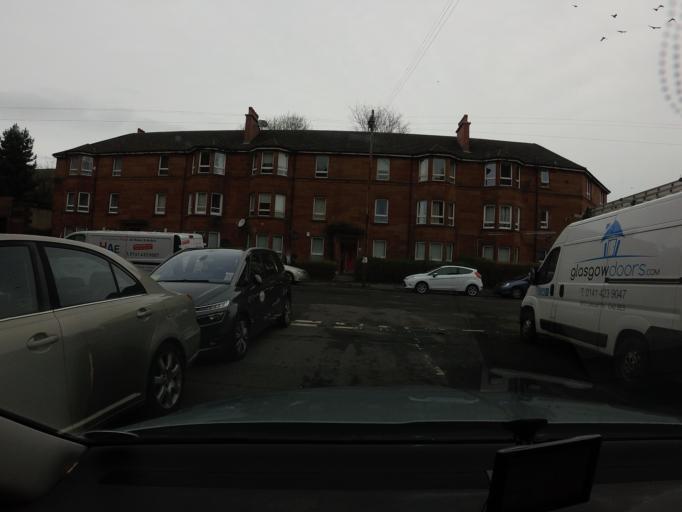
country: GB
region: Scotland
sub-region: Glasgow City
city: Glasgow
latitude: 55.8333
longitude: -4.2542
